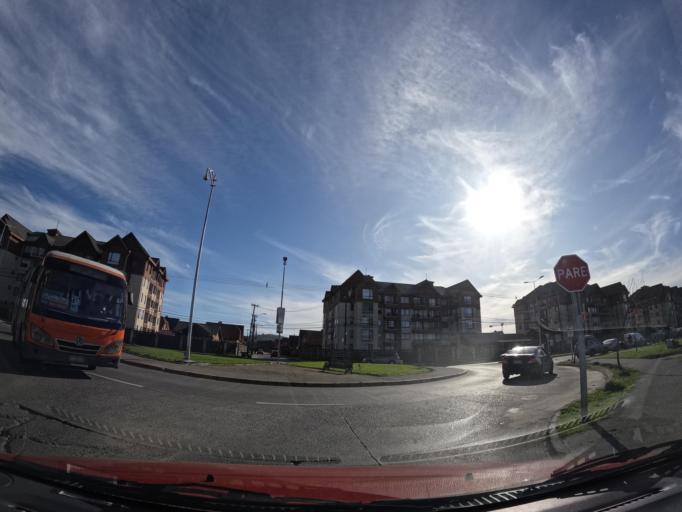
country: CL
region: Biobio
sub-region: Provincia de Concepcion
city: Talcahuano
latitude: -36.7695
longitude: -73.0754
